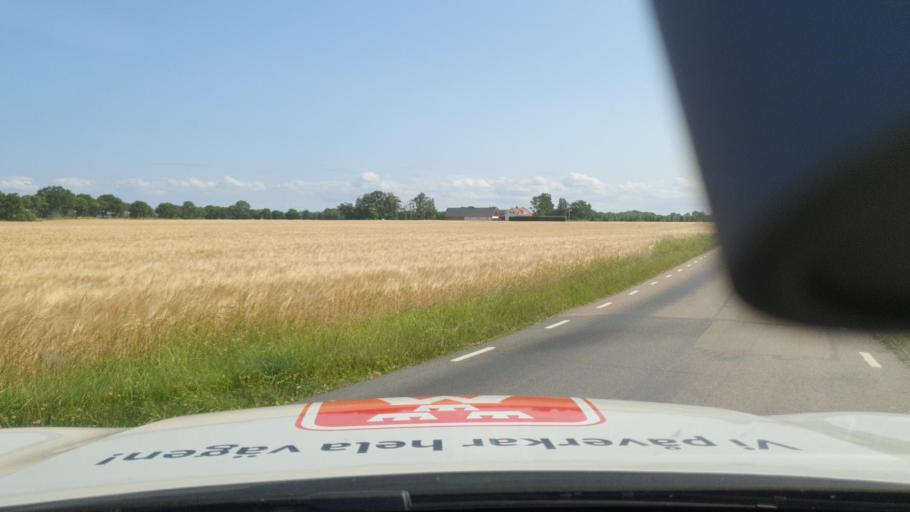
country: SE
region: Skane
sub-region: Hoganas Kommun
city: Hoganas
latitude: 56.2222
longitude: 12.6457
